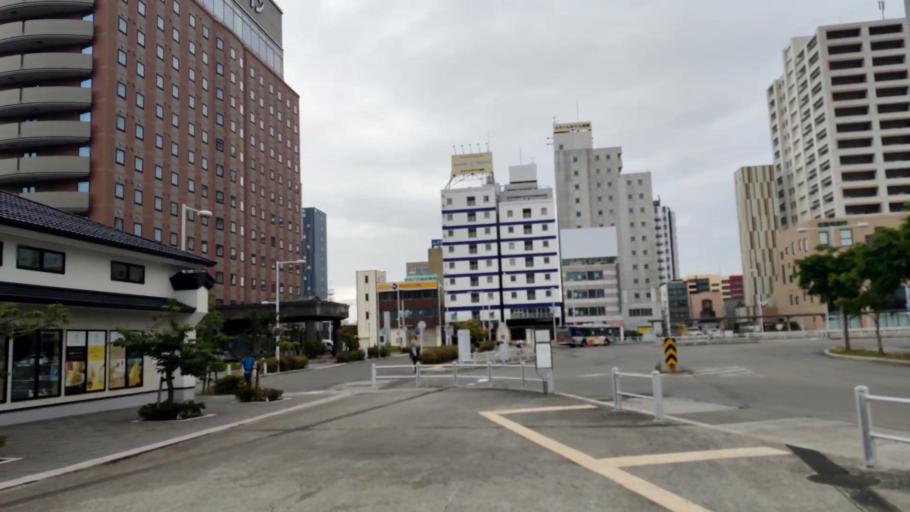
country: JP
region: Hokkaido
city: Hakodate
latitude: 41.7740
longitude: 140.7273
